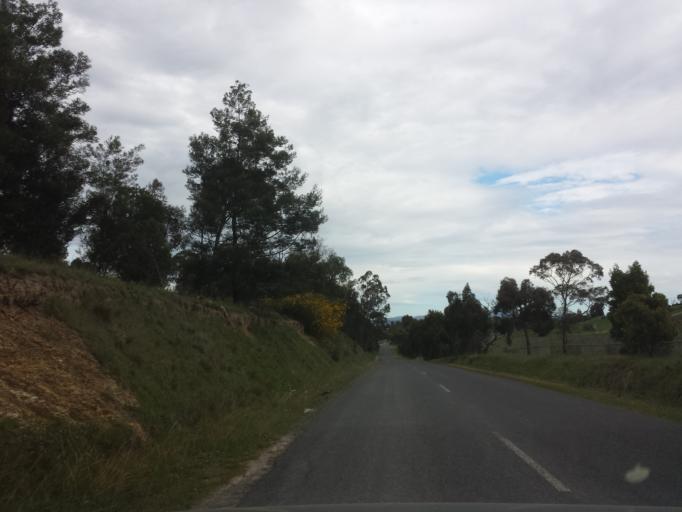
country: AU
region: Victoria
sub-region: Yarra Ranges
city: Yarra Glen
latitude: -37.6353
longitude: 145.3740
